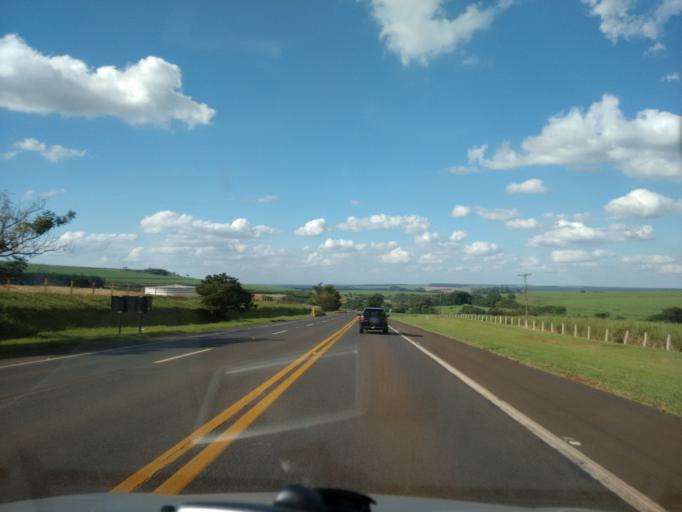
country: BR
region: Sao Paulo
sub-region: Americo Brasiliense
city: Americo Brasiliense
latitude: -21.7626
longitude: -48.0796
